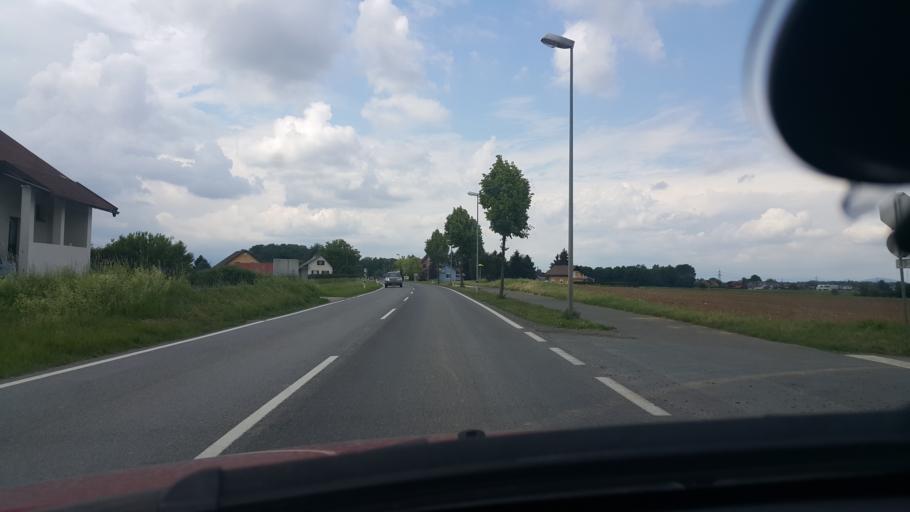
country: AT
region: Styria
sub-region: Politischer Bezirk Leibnitz
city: Weitendorf
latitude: 46.8872
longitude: 15.4872
